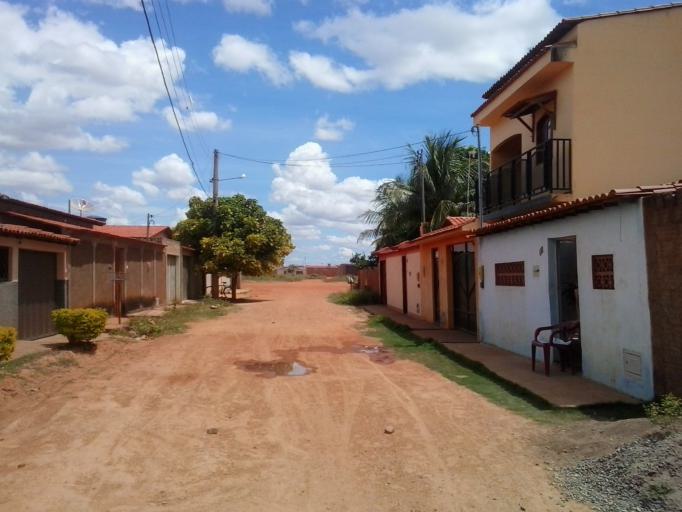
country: BR
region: Bahia
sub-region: Livramento Do Brumado
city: Livramento do Brumado
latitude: -13.6599
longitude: -41.8515
